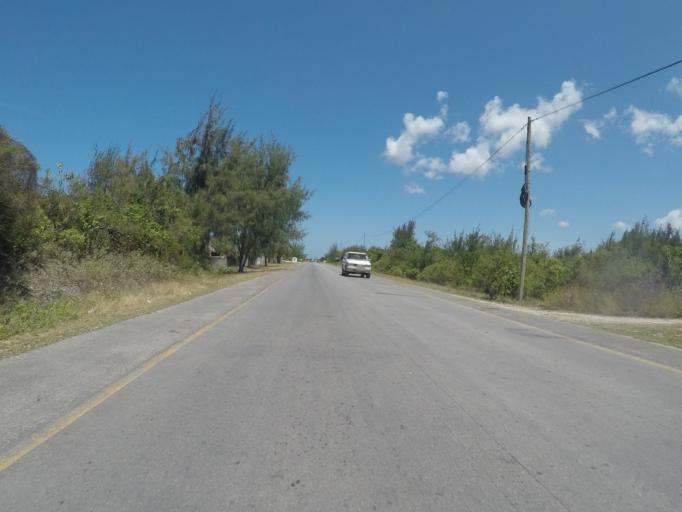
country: TZ
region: Zanzibar Central/South
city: Nganane
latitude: -6.2854
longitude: 39.5362
